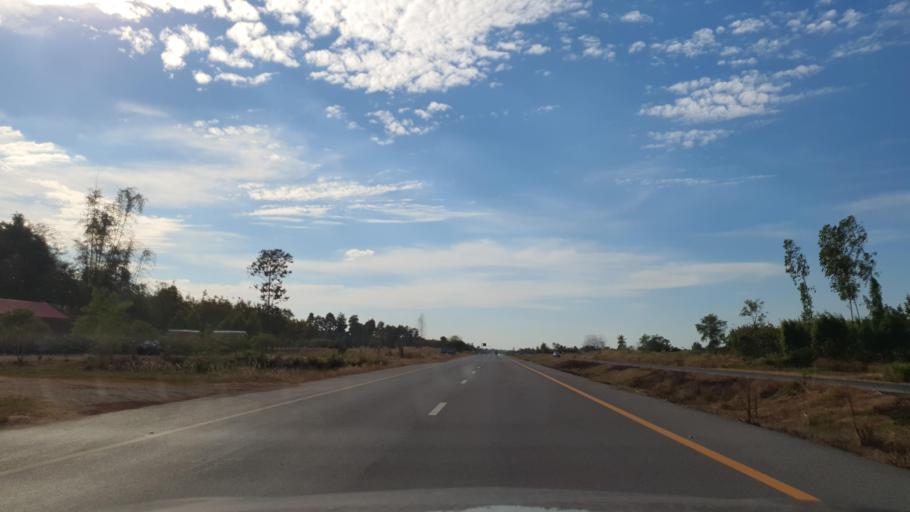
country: TH
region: Roi Et
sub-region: Amphoe Pho Chai
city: Pho Chai
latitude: 16.4127
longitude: 103.7722
